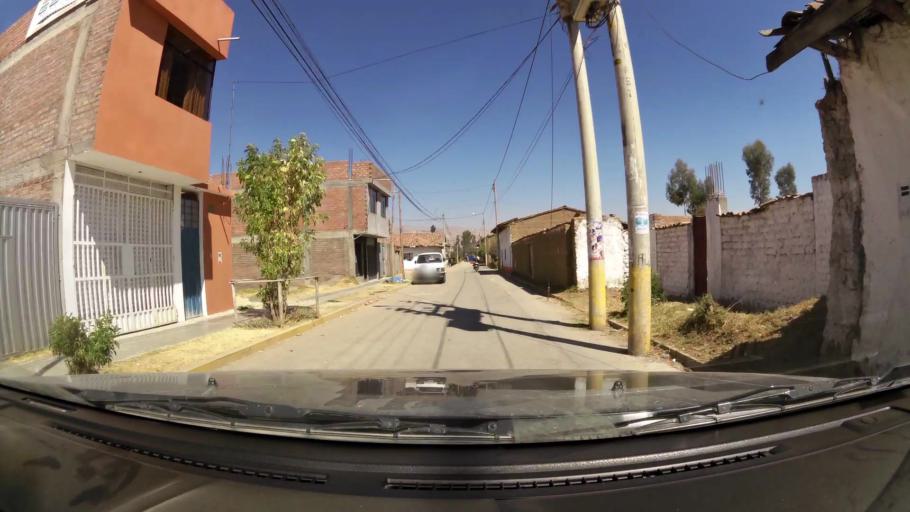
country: PE
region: Junin
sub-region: Provincia de Concepcion
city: Concepcion
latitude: -11.9149
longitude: -75.3184
